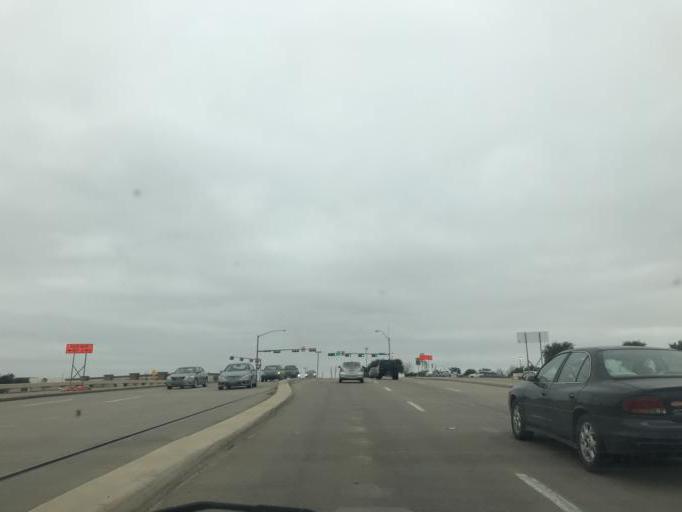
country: US
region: Texas
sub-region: Dallas County
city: Irving
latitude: 32.8646
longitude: -97.0025
